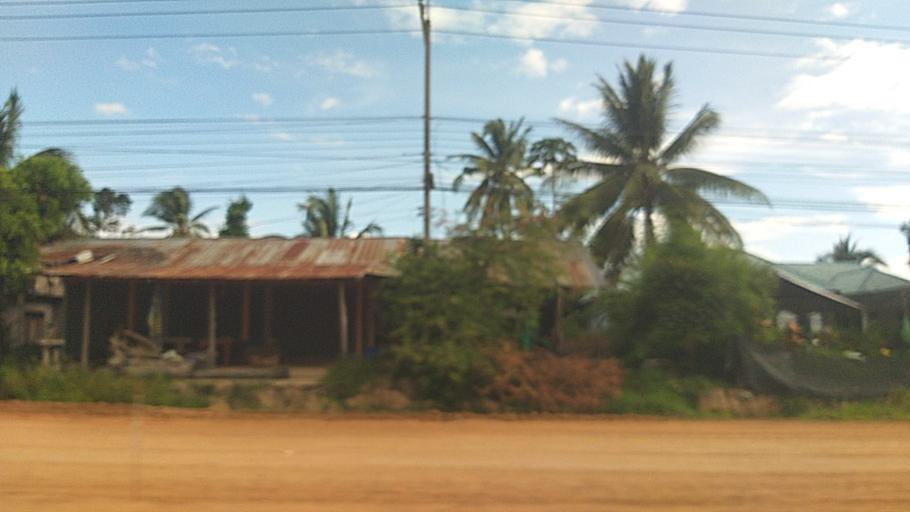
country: TH
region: Surin
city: Kap Choeng
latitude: 14.4712
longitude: 103.6142
